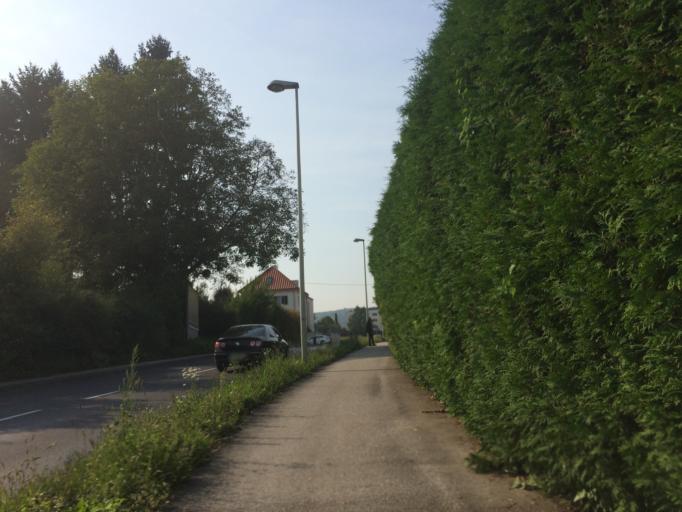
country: AT
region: Upper Austria
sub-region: Politischer Bezirk Linz-Land
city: Leonding
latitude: 48.2771
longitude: 14.2479
